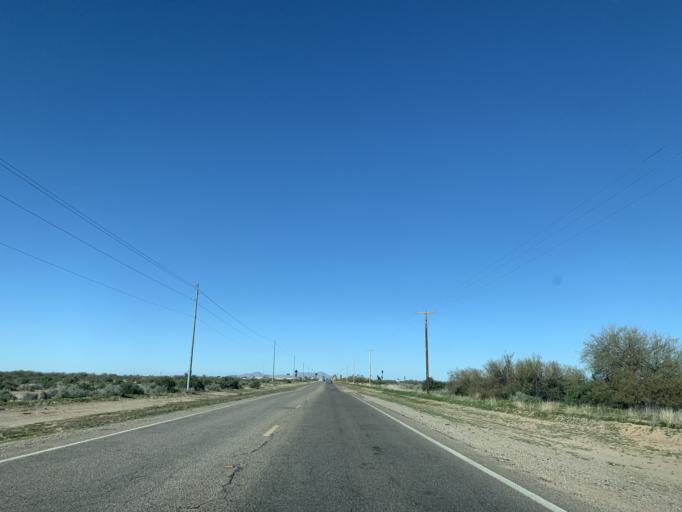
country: US
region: Arizona
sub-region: Pinal County
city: Arizona City
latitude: 32.7948
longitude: -111.6710
